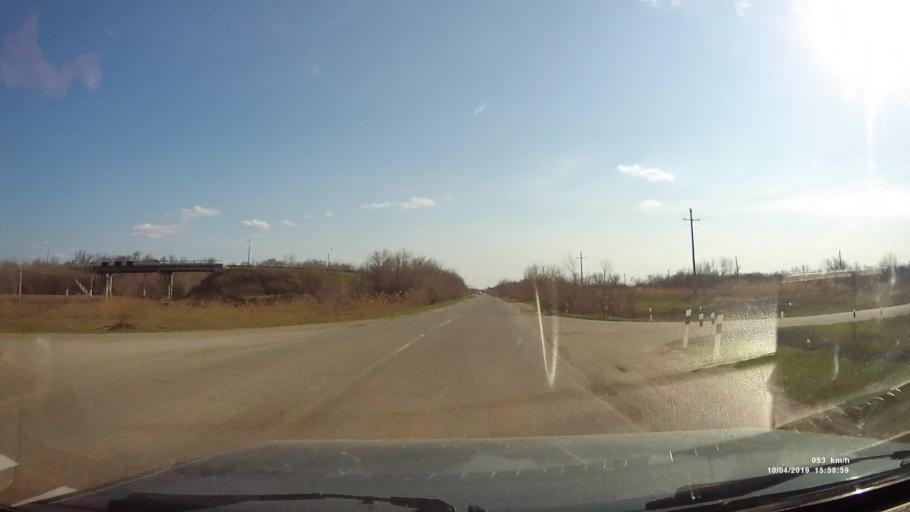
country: RU
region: Rostov
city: Masalovka
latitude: 48.3981
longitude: 40.2704
